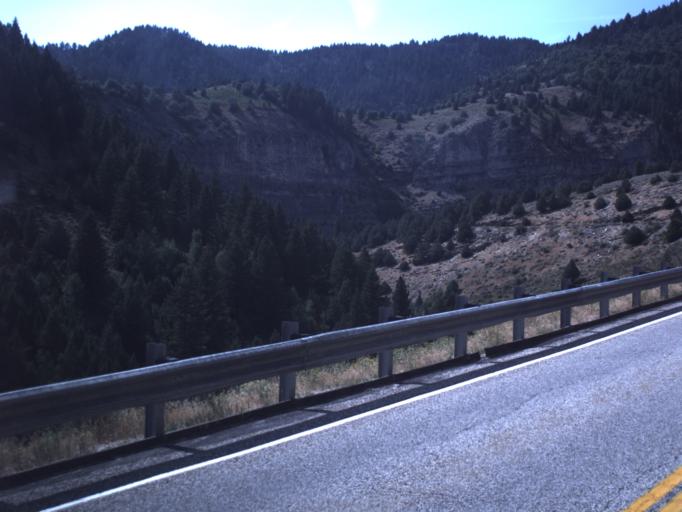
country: US
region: Utah
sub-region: Cache County
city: North Logan
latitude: 41.8275
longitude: -111.6017
